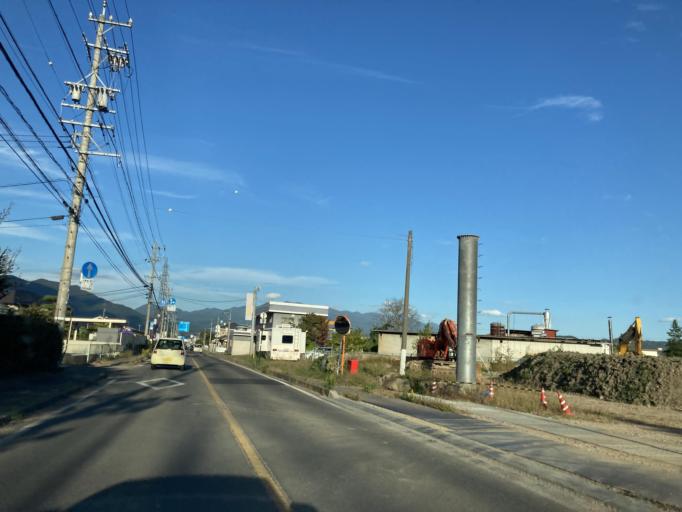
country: JP
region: Nagano
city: Ueda
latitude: 36.3818
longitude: 138.1823
